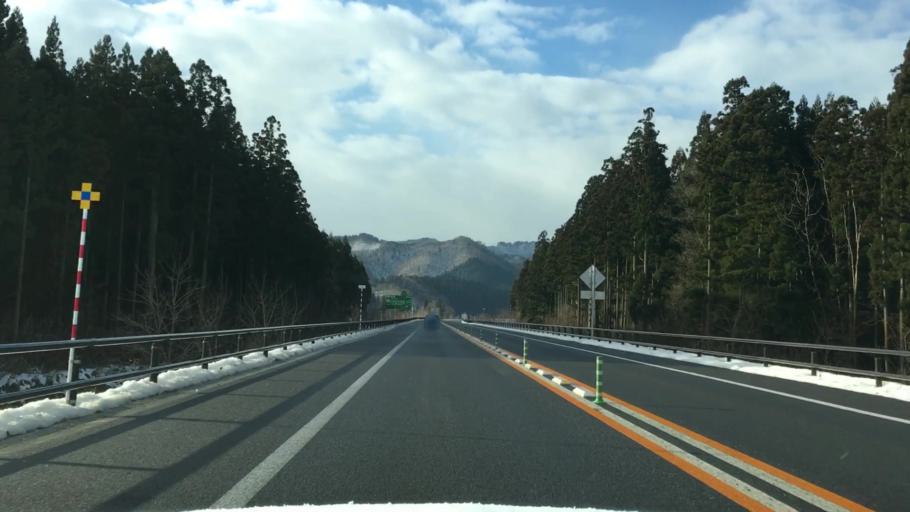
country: JP
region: Akita
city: Odate
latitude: 40.2414
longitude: 140.5068
